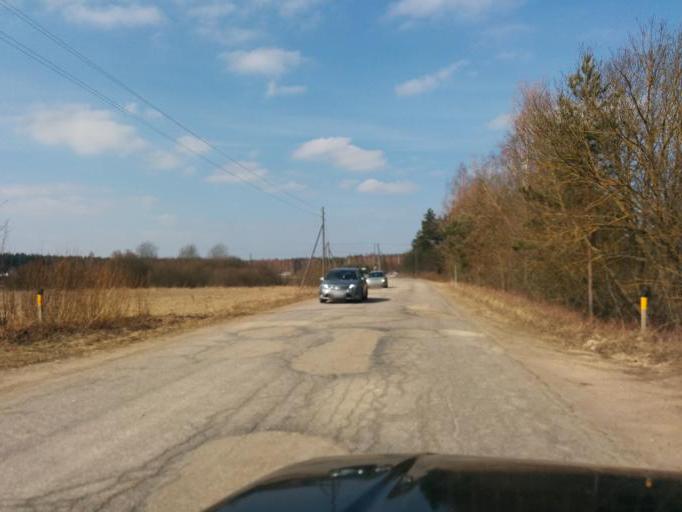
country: LV
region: Kekava
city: Kekava
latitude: 56.8489
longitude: 24.2415
